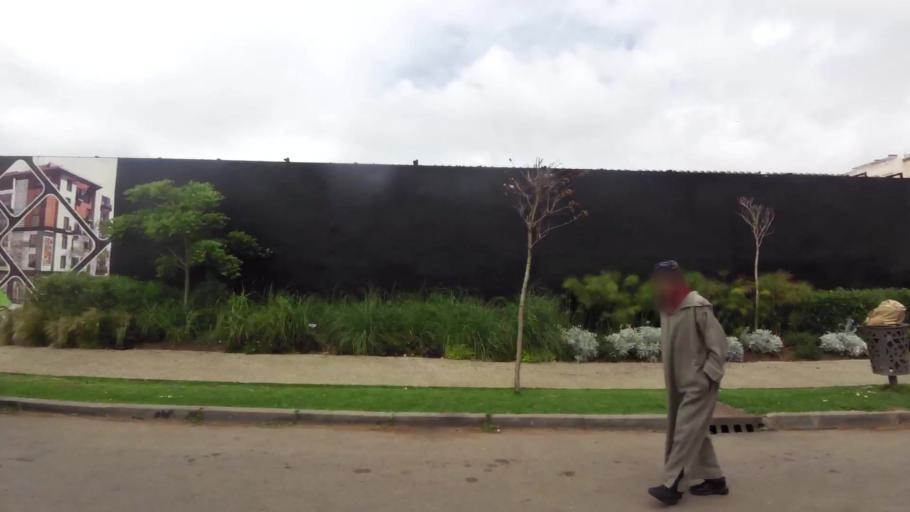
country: MA
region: Grand Casablanca
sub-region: Casablanca
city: Casablanca
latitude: 33.6006
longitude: -7.6505
